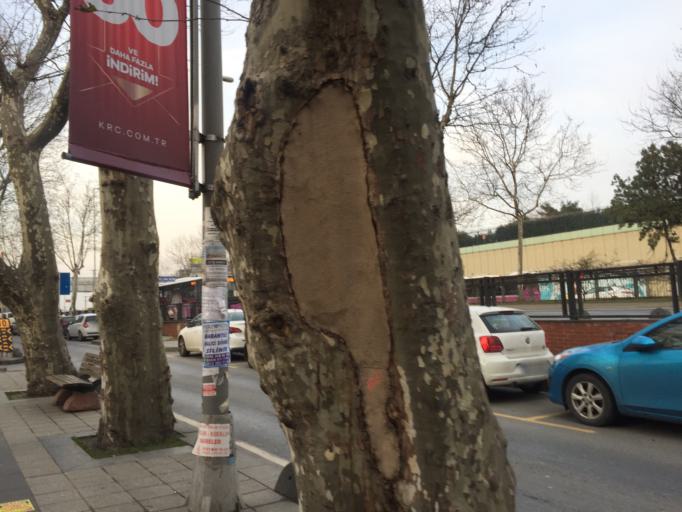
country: TR
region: Istanbul
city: Sisli
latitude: 41.0889
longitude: 29.0059
